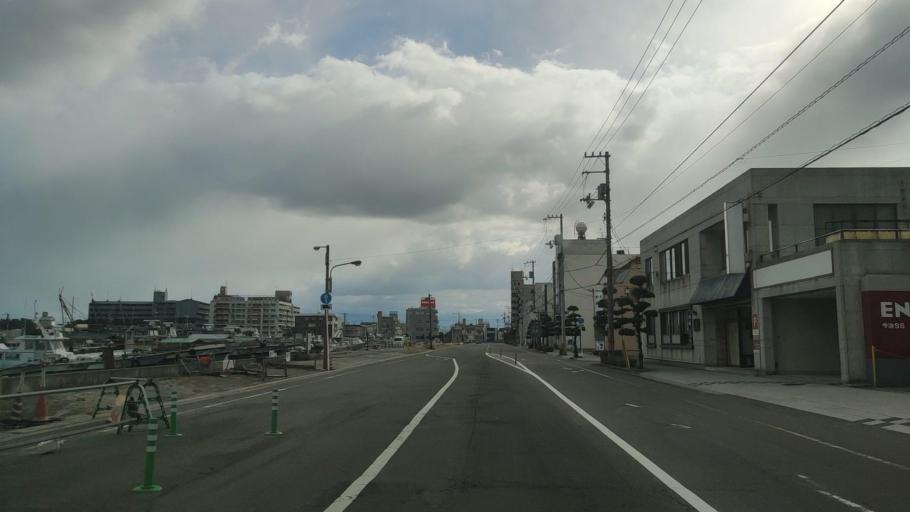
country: JP
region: Ehime
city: Saijo
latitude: 34.0681
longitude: 133.0049
